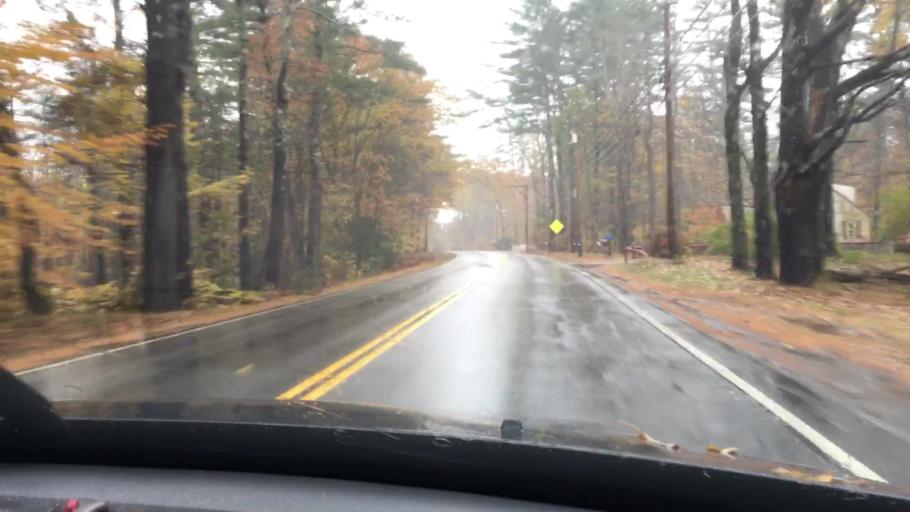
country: US
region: New Hampshire
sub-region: Belknap County
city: Meredith
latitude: 43.7042
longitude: -71.5202
